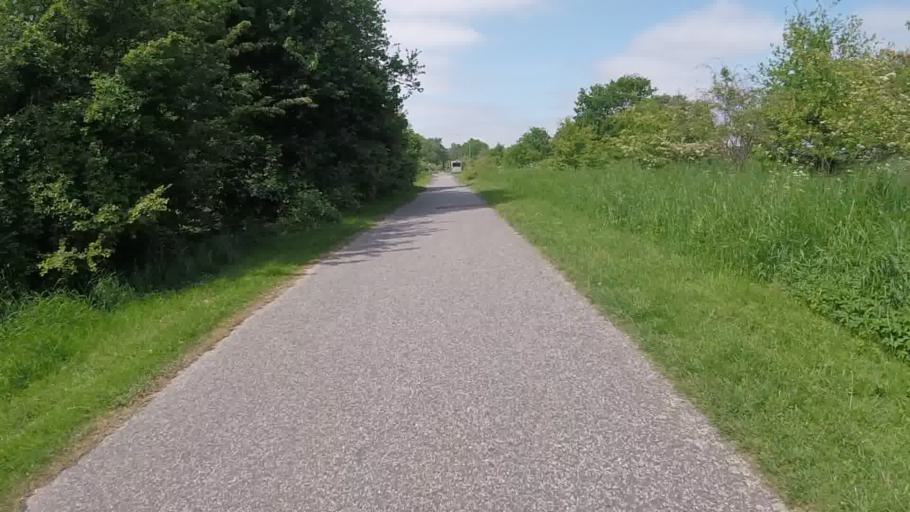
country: DE
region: Schleswig-Holstein
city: Oststeinbek
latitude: 53.4905
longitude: 10.1605
